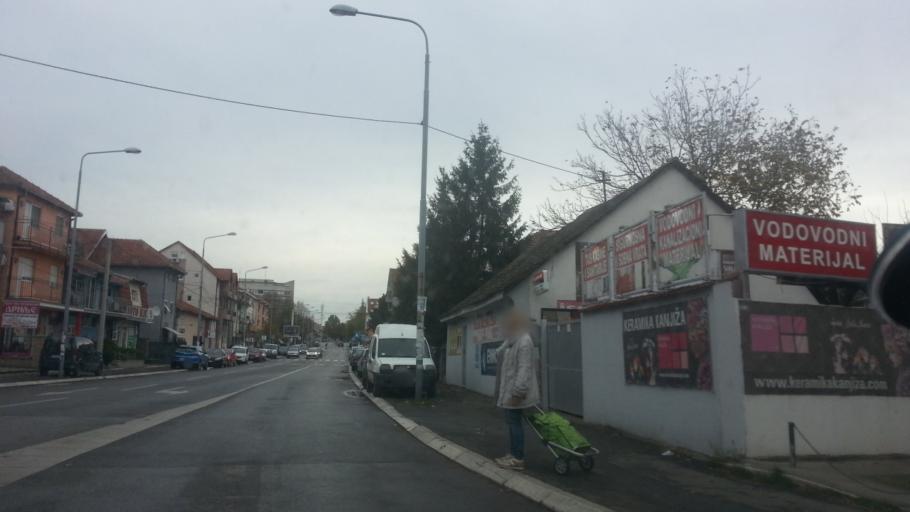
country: RS
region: Central Serbia
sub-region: Belgrade
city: Zemun
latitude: 44.8427
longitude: 20.3938
